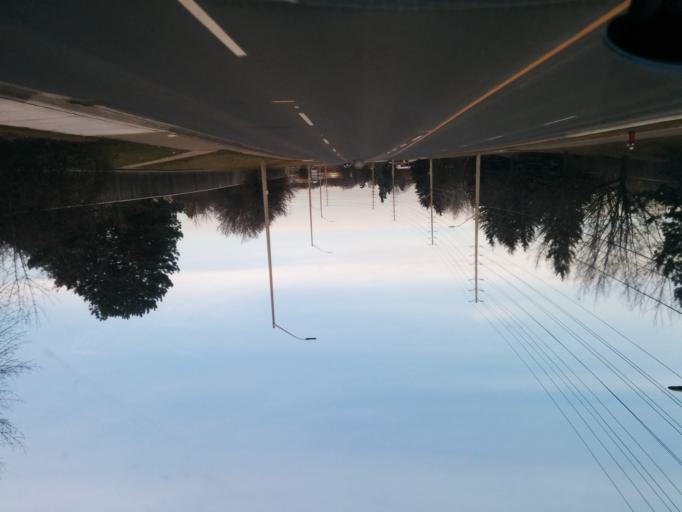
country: CA
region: Ontario
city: Mississauga
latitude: 43.5407
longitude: -79.6951
